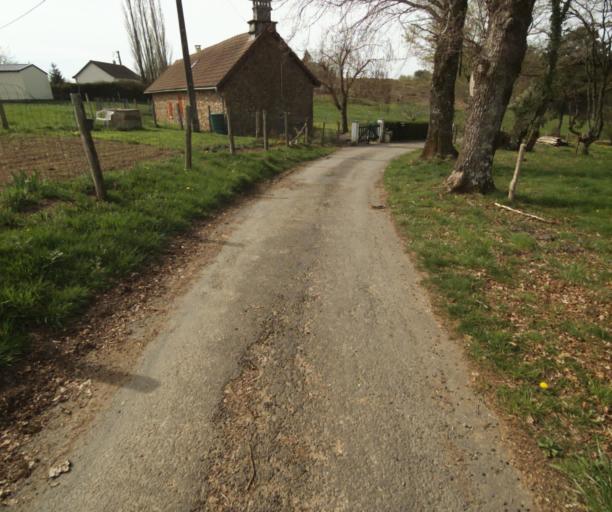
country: FR
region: Limousin
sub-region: Departement de la Correze
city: Correze
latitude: 45.3699
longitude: 1.8197
